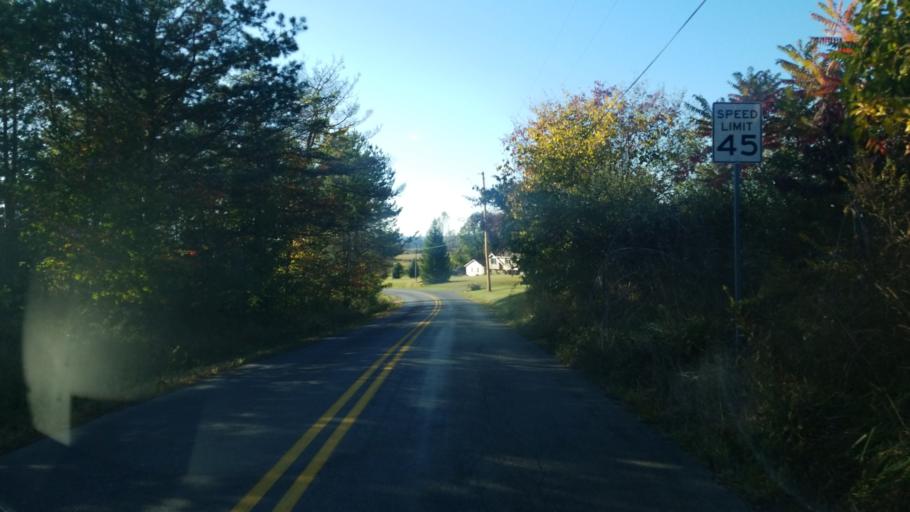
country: US
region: Pennsylvania
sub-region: Indiana County
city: Johnsonburg
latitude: 40.9028
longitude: -78.9047
